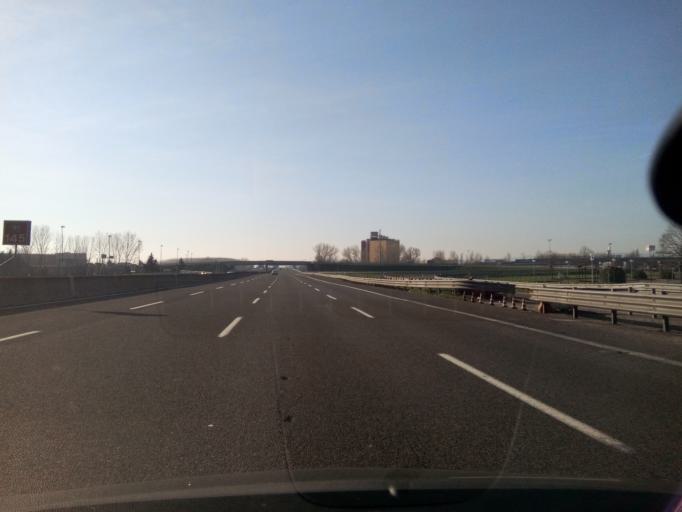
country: IT
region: Emilia-Romagna
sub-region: Provincia di Modena
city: Campogalliano
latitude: 44.6568
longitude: 10.8610
